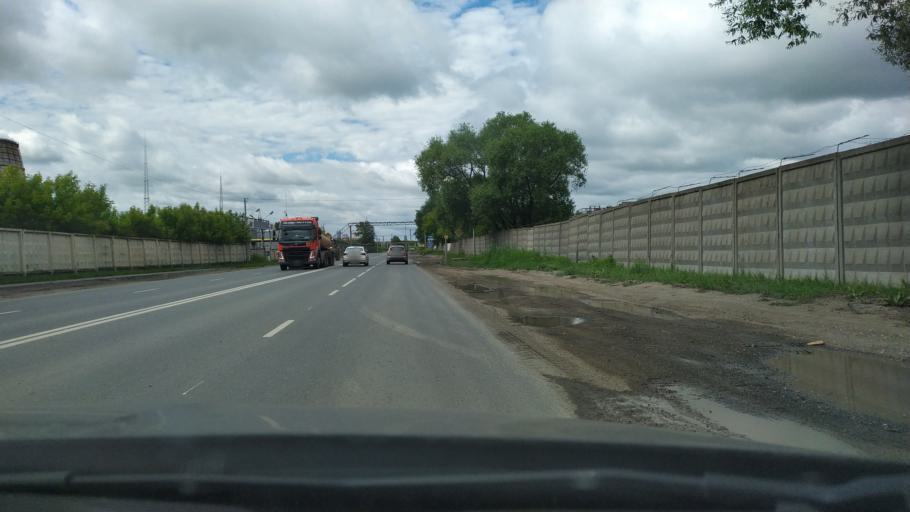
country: RU
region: Perm
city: Kondratovo
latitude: 57.9299
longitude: 56.1450
